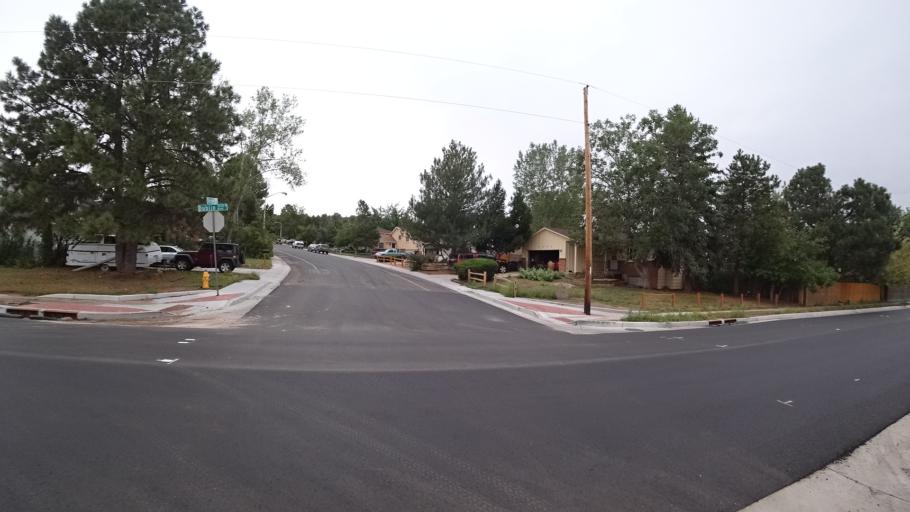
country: US
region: Colorado
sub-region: El Paso County
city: Colorado Springs
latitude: 38.9251
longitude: -104.8003
